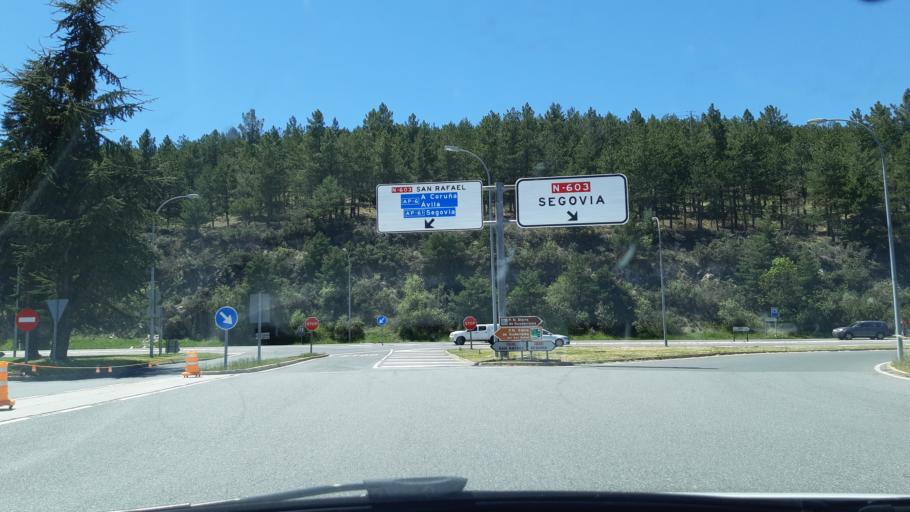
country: ES
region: Castille and Leon
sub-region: Provincia de Segovia
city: Otero de Herreros
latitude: 40.7276
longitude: -4.1962
